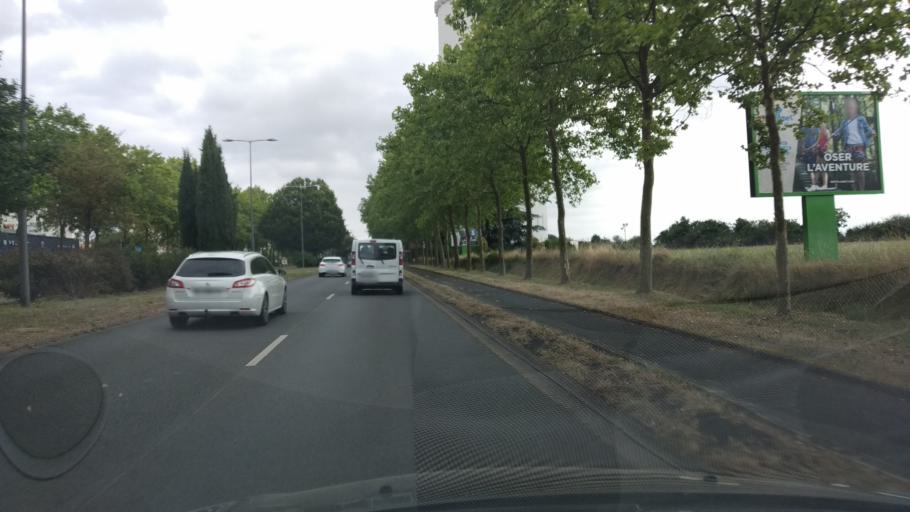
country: FR
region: Poitou-Charentes
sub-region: Departement de la Vienne
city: Saint-Benoit
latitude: 46.5631
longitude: 0.3470
